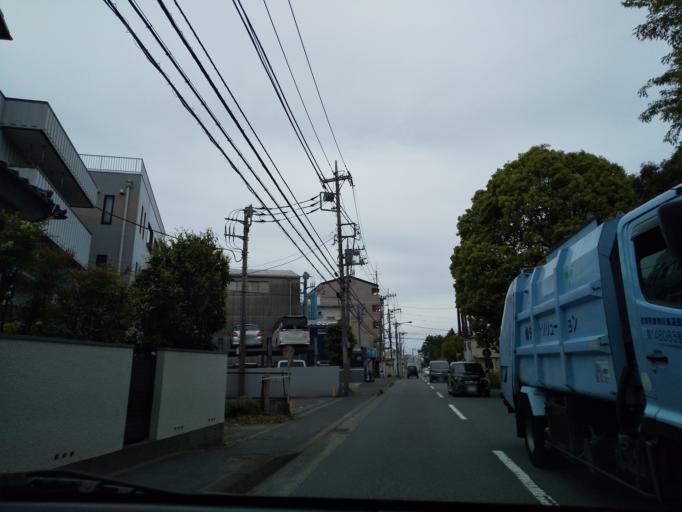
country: JP
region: Tokyo
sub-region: Machida-shi
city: Machida
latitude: 35.5507
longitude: 139.3996
